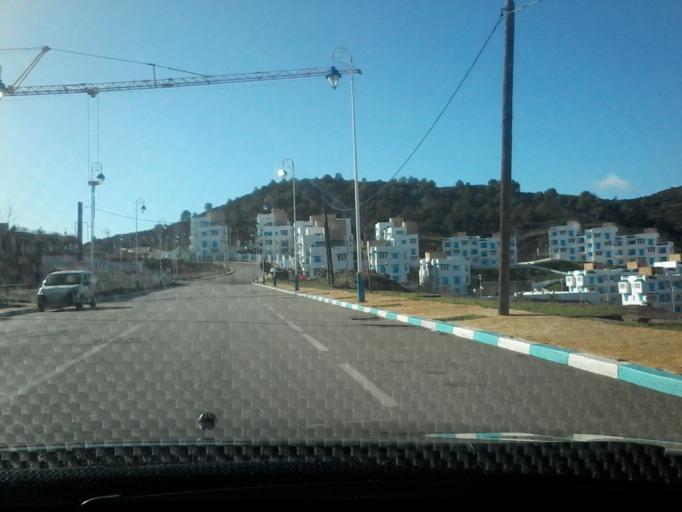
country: MA
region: Tanger-Tetouan
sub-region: Tetouan
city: Martil
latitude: 35.6764
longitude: -5.3258
